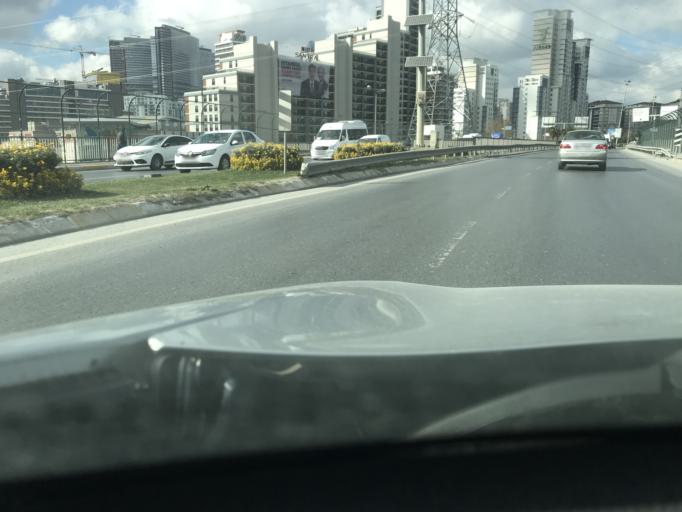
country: TR
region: Istanbul
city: Esenyurt
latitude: 41.0534
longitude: 28.6703
